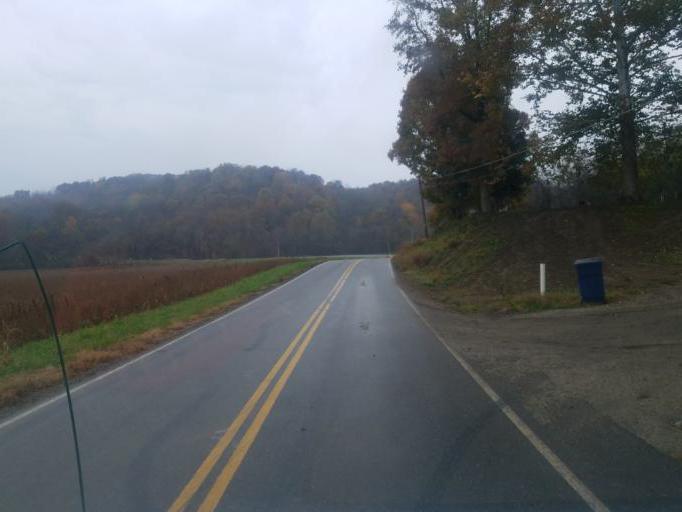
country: US
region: Ohio
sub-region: Morgan County
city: McConnelsville
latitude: 39.5559
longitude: -81.7941
